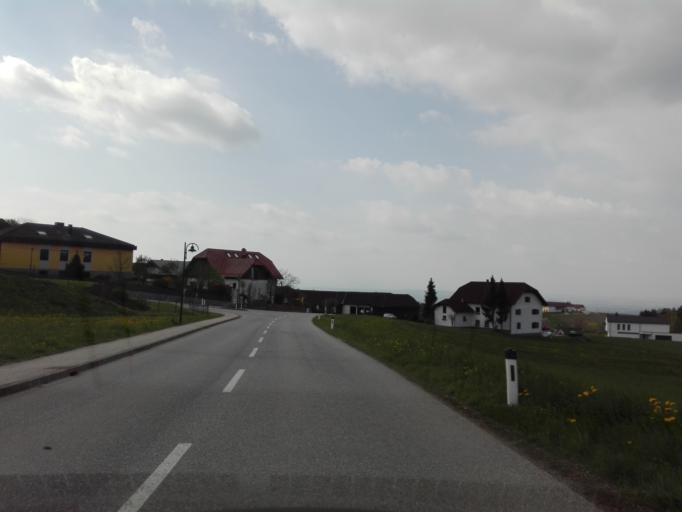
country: AT
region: Upper Austria
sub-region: Politischer Bezirk Perg
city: Perg
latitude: 48.2835
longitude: 14.6784
